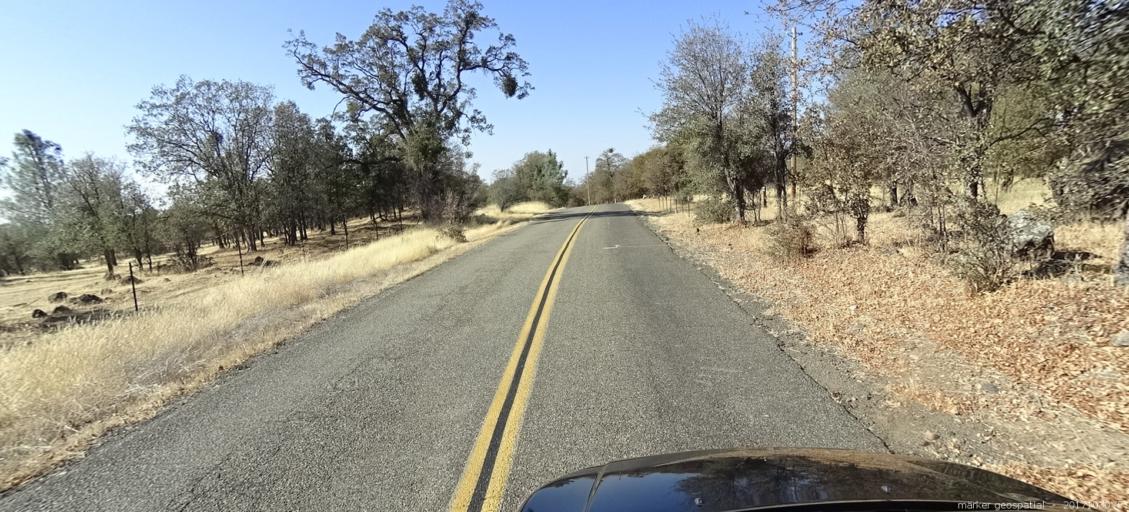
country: US
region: California
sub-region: Shasta County
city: Shingletown
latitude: 40.6459
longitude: -121.9409
